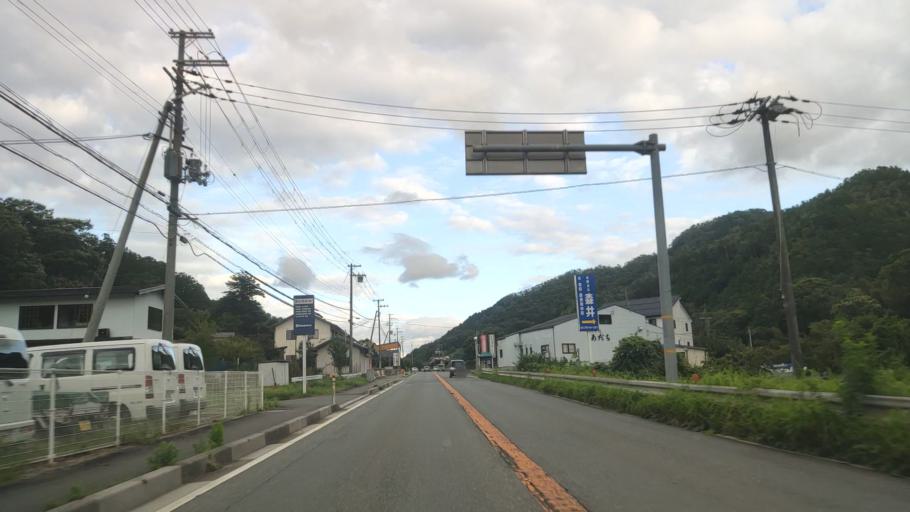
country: JP
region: Hyogo
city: Toyooka
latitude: 35.3724
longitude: 134.7906
